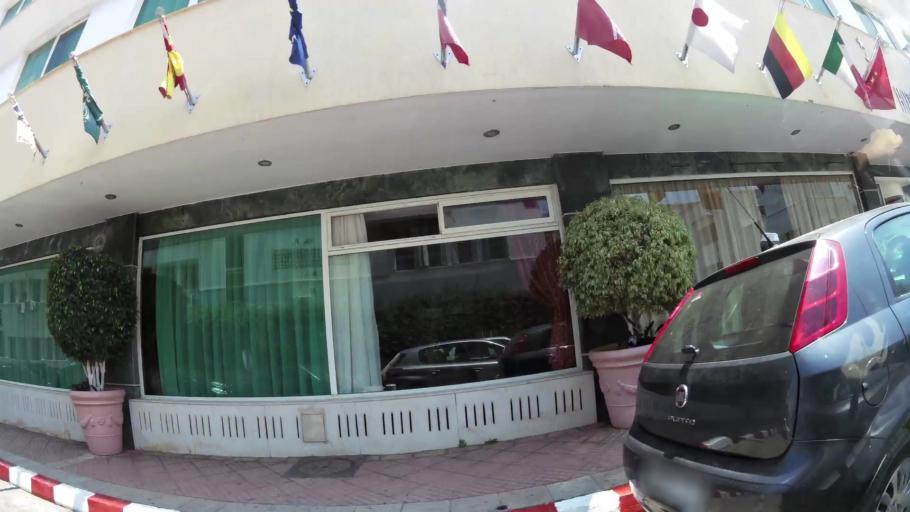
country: MA
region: Rabat-Sale-Zemmour-Zaer
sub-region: Rabat
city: Rabat
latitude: 34.0143
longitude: -6.8318
